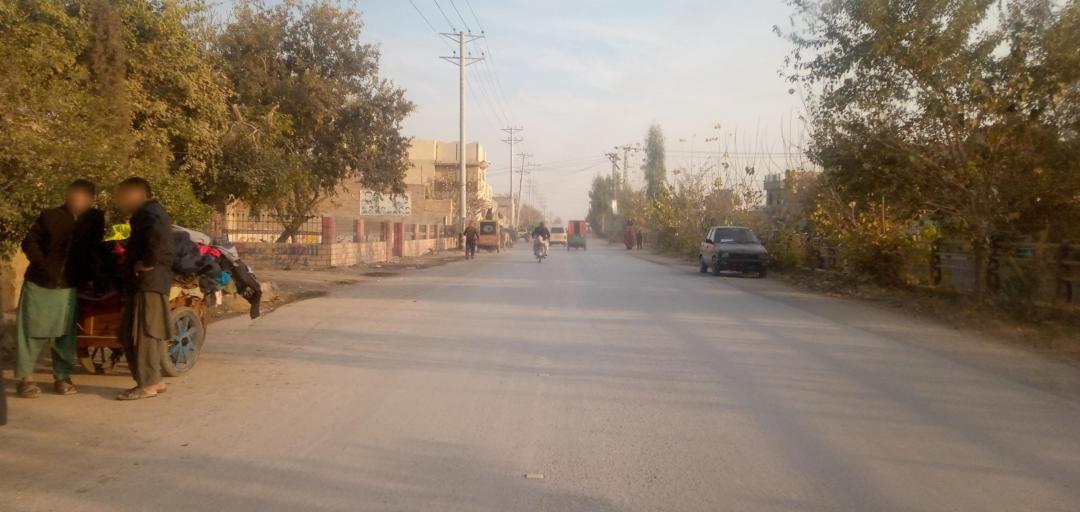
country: PK
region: Khyber Pakhtunkhwa
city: Peshawar
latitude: 33.9721
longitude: 71.5322
